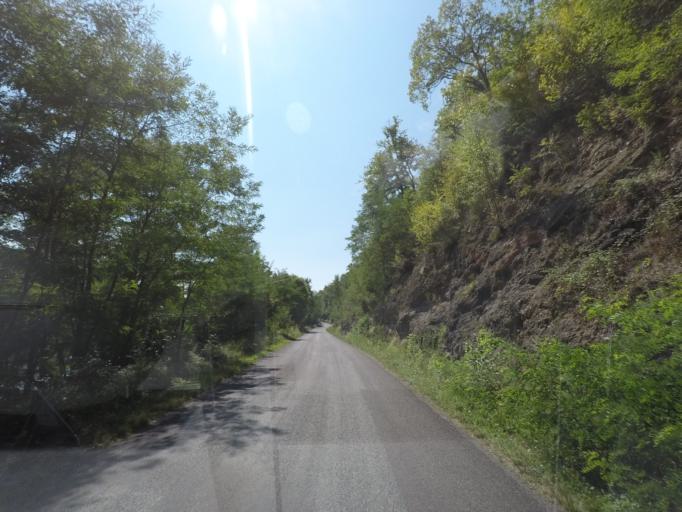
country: FR
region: Midi-Pyrenees
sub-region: Departement de l'Aveyron
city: Livinhac-le-Haut
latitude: 44.6063
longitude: 2.2310
